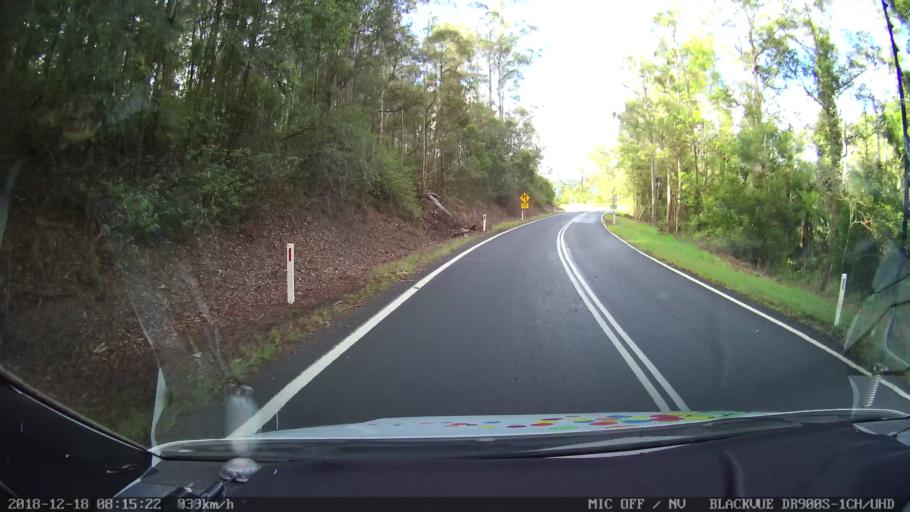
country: AU
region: New South Wales
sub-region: Kyogle
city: Kyogle
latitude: -28.3357
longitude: 152.6868
